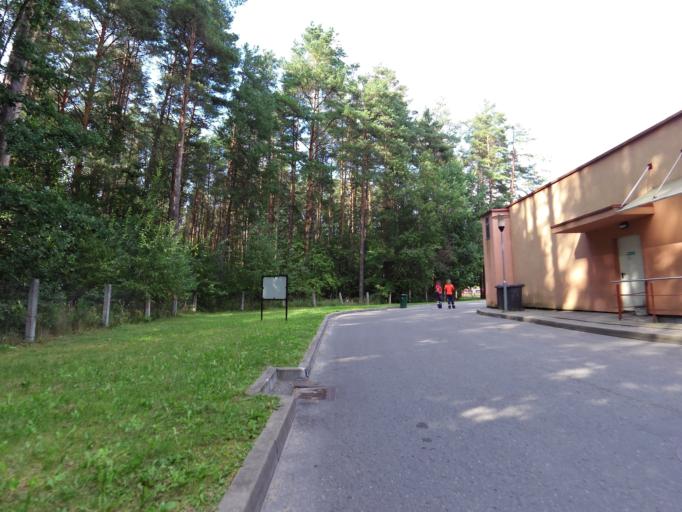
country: LT
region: Vilnius County
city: Lazdynai
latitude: 54.6677
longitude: 25.2051
